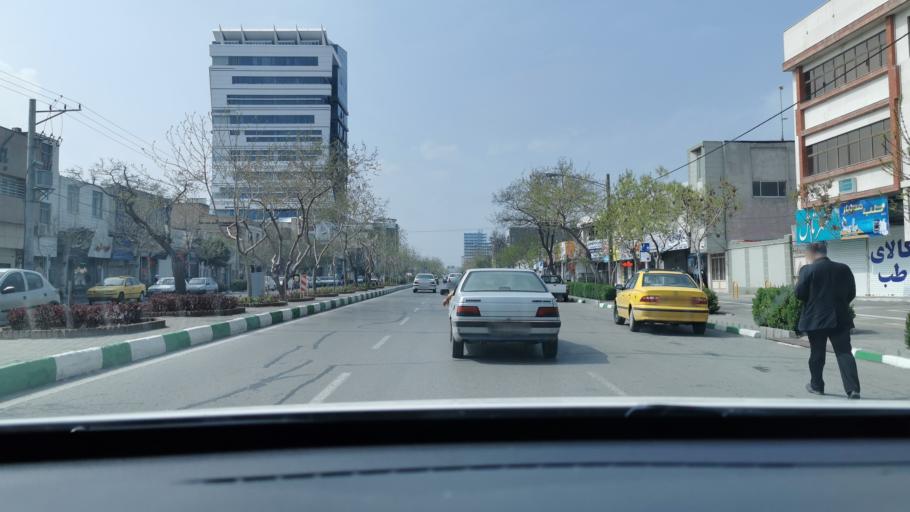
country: IR
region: Razavi Khorasan
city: Mashhad
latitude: 36.3295
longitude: 59.5249
